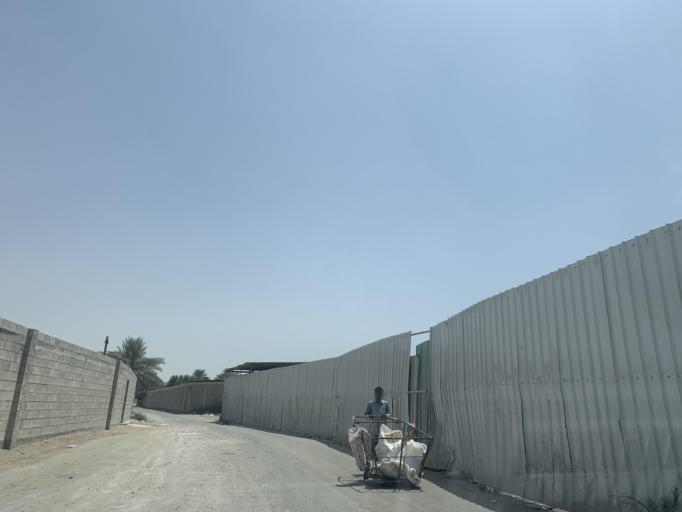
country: BH
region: Central Governorate
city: Madinat Hamad
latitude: 26.1605
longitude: 50.4946
